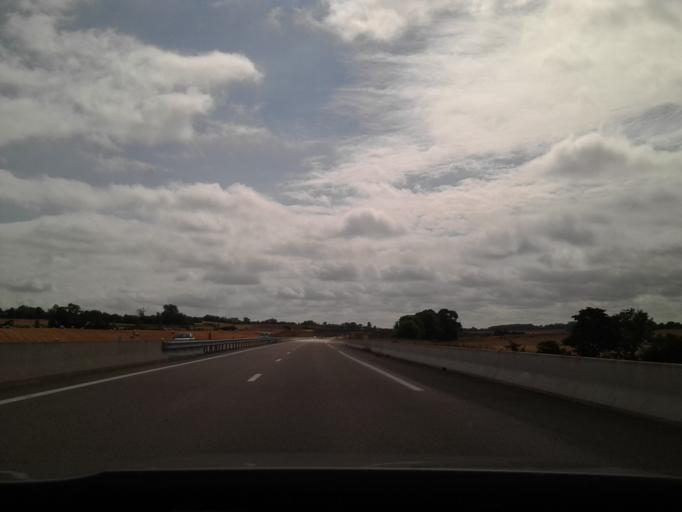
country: FR
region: Lower Normandy
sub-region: Departement de l'Orne
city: Argentan
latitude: 48.6904
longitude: -0.0022
